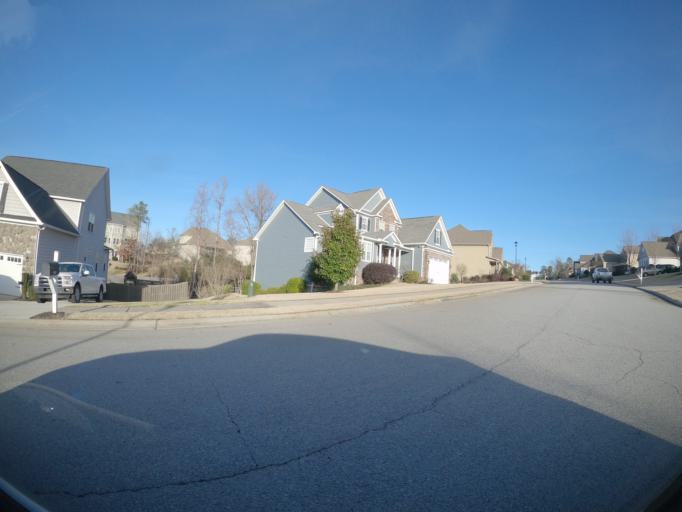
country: US
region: Georgia
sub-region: Columbia County
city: Evans
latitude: 33.5889
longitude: -82.2007
